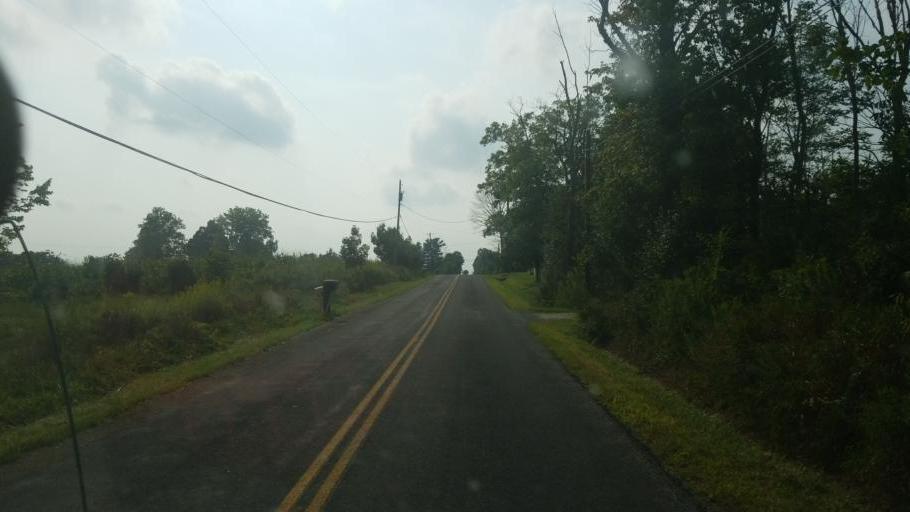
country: US
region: Ohio
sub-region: Medina County
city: Westfield Center
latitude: 41.0518
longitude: -81.9372
